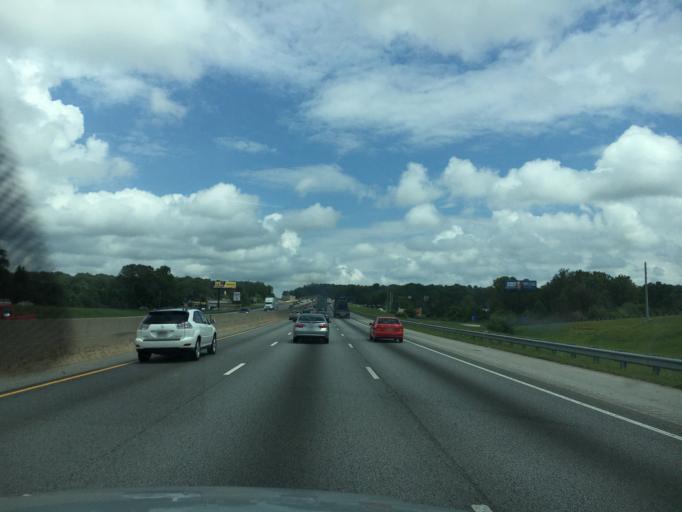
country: US
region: Georgia
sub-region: DeKalb County
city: Lithonia
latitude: 33.7022
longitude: -84.1230
